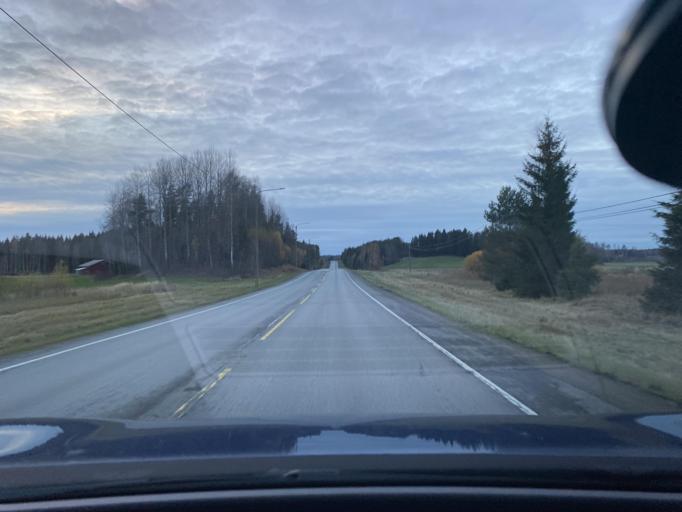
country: FI
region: Uusimaa
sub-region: Helsinki
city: Saukkola
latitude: 60.3858
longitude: 24.0639
